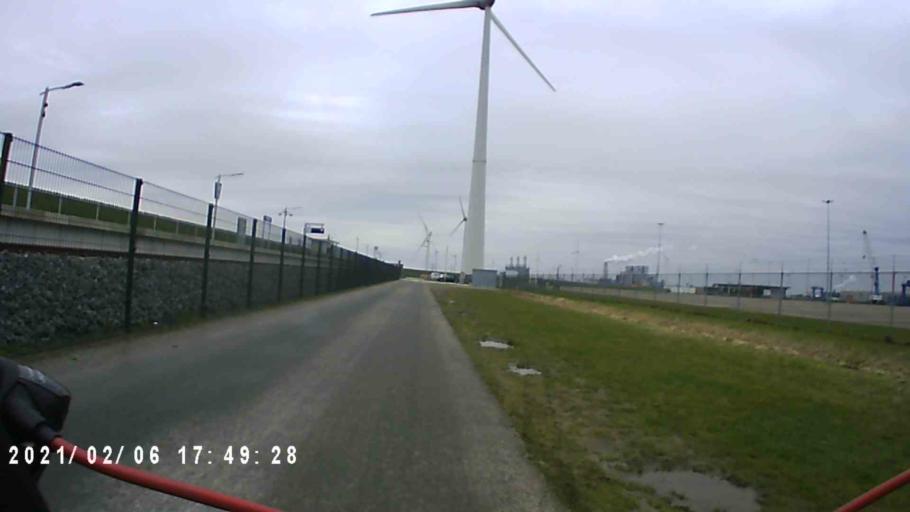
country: NL
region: Groningen
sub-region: Gemeente Appingedam
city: Appingedam
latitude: 53.4587
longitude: 6.8302
